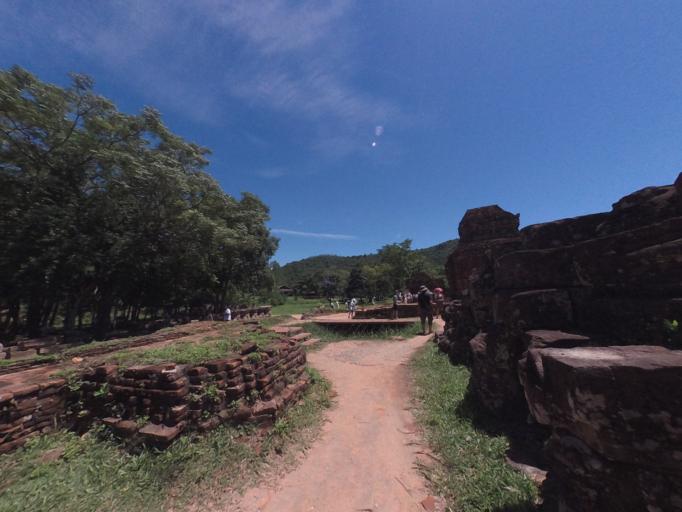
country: VN
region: Quang Nam
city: Dai Loc
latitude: 15.7630
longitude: 108.1239
